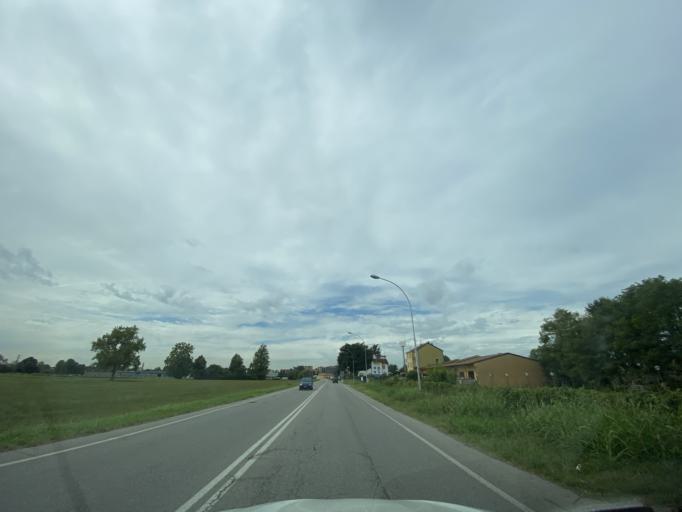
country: IT
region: Lombardy
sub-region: Citta metropolitana di Milano
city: Sant'Agata Martesana
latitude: 45.5222
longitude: 9.3754
